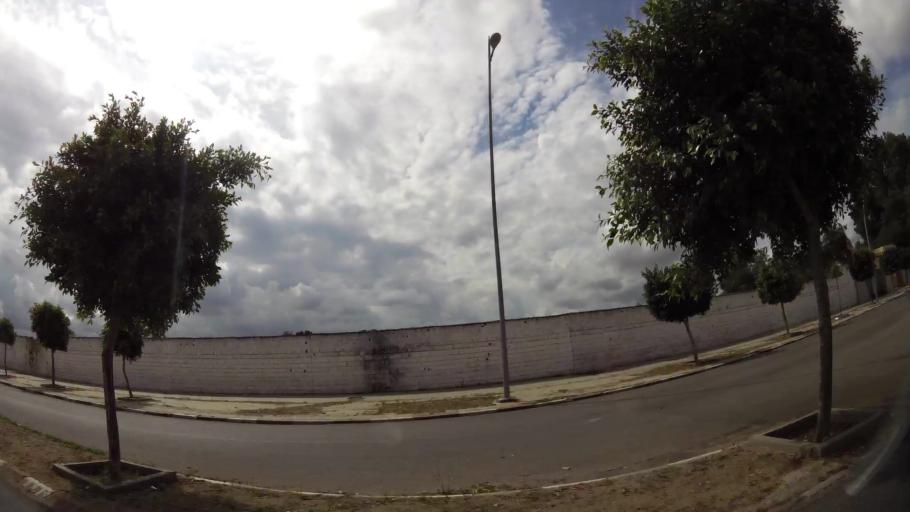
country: MA
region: Gharb-Chrarda-Beni Hssen
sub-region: Kenitra Province
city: Kenitra
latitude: 34.2581
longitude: -6.5669
